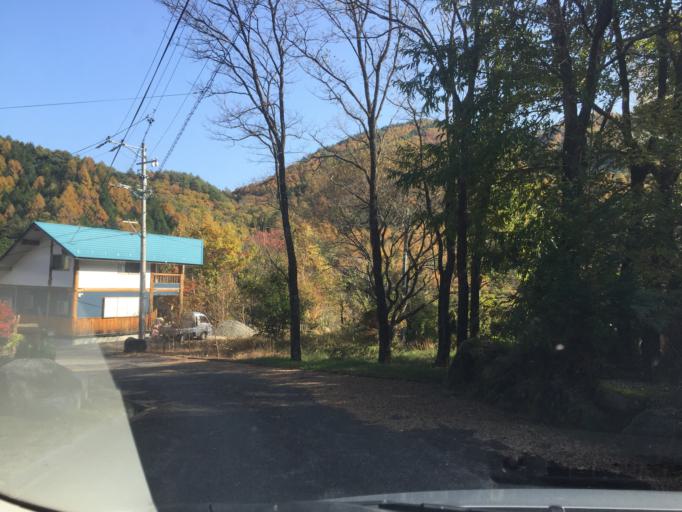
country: JP
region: Gifu
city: Nakatsugawa
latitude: 35.3694
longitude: 137.6742
